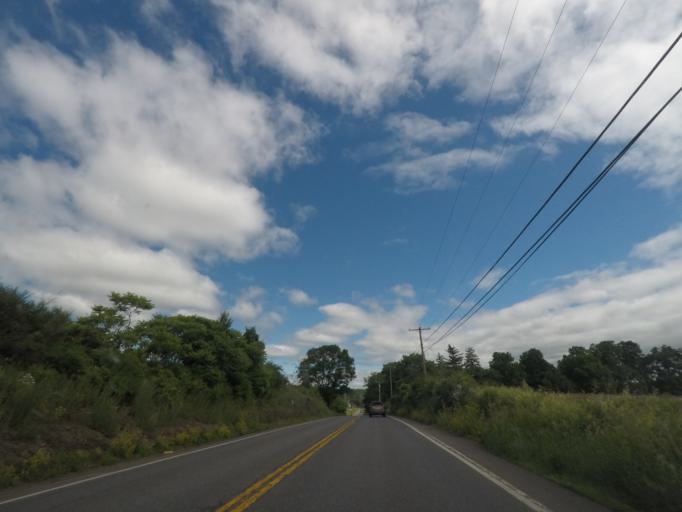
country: US
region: New York
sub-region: Columbia County
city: Philmont
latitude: 42.2148
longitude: -73.7057
